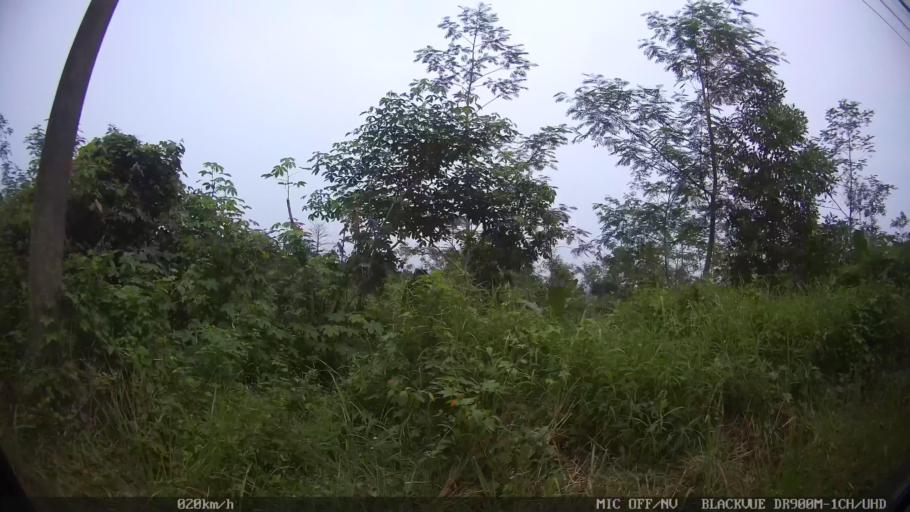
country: ID
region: Lampung
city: Panjang
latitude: -5.4341
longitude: 105.3076
